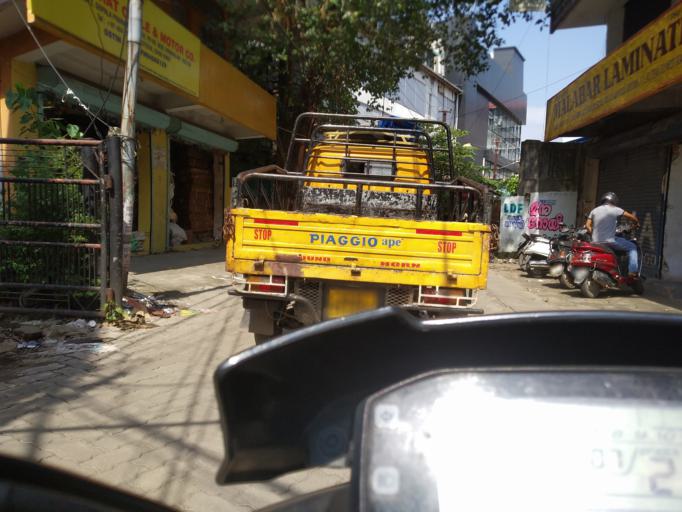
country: IN
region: Kerala
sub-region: Ernakulam
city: Cochin
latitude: 9.9791
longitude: 76.2825
